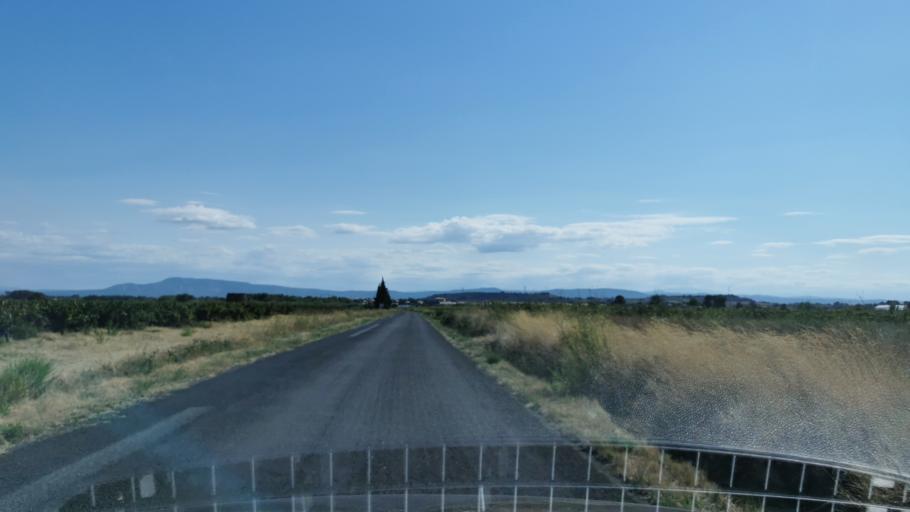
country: FR
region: Languedoc-Roussillon
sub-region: Departement de l'Aude
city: Peyriac-Minervois
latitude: 43.3063
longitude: 2.5639
